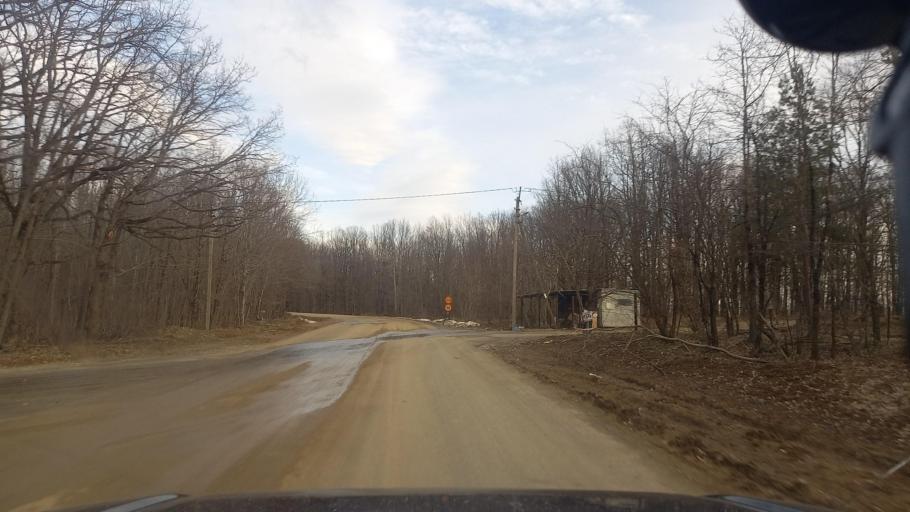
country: RU
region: Krasnodarskiy
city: Goryachiy Klyuch
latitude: 44.6992
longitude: 39.0223
